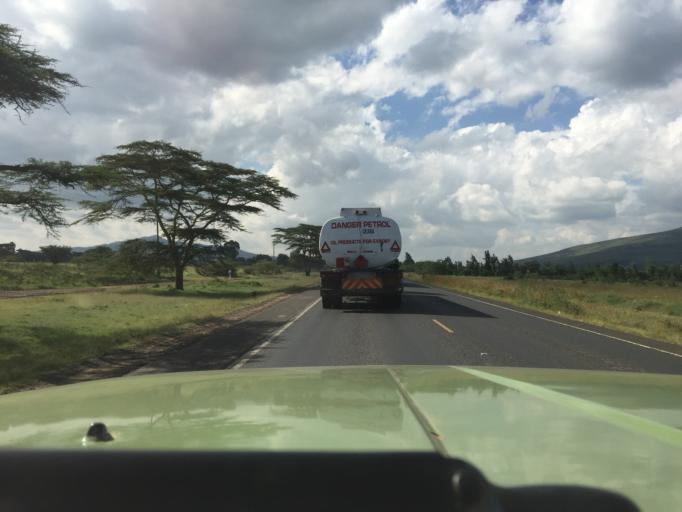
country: KE
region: Nakuru
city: Kijabe
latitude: -0.9606
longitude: 36.5596
